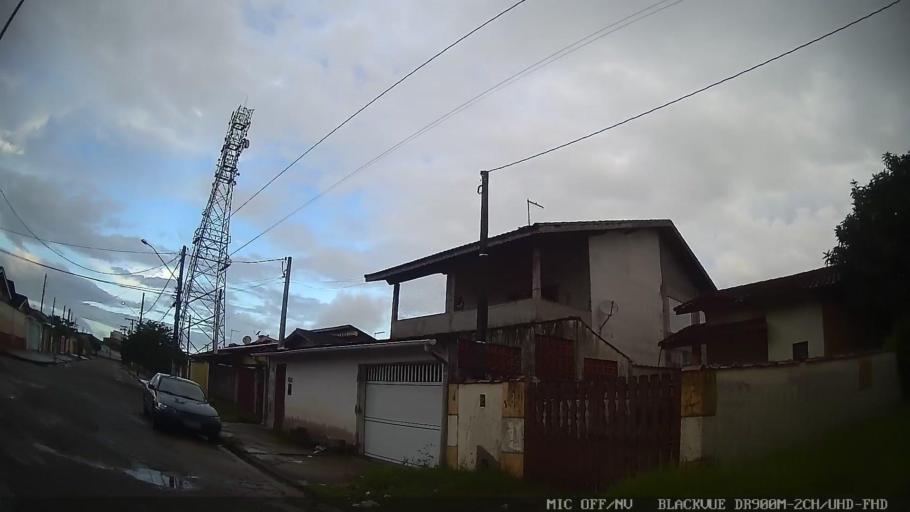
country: BR
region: Sao Paulo
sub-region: Itanhaem
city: Itanhaem
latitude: -24.1775
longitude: -46.7923
